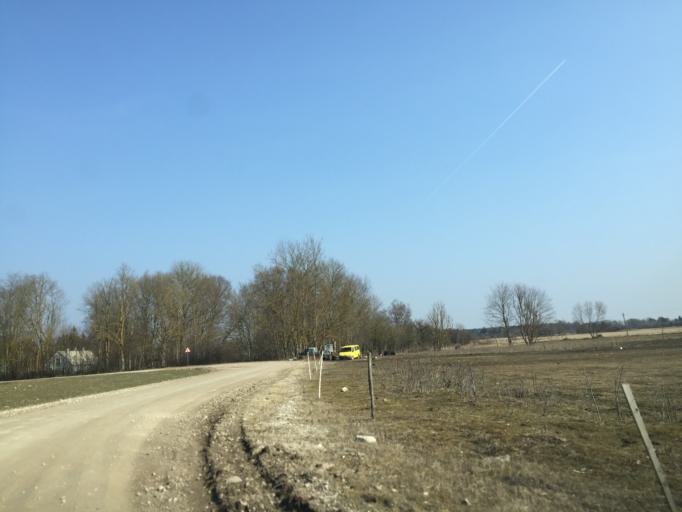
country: EE
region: Saare
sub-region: Kuressaare linn
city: Kuressaare
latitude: 58.3795
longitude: 22.6895
